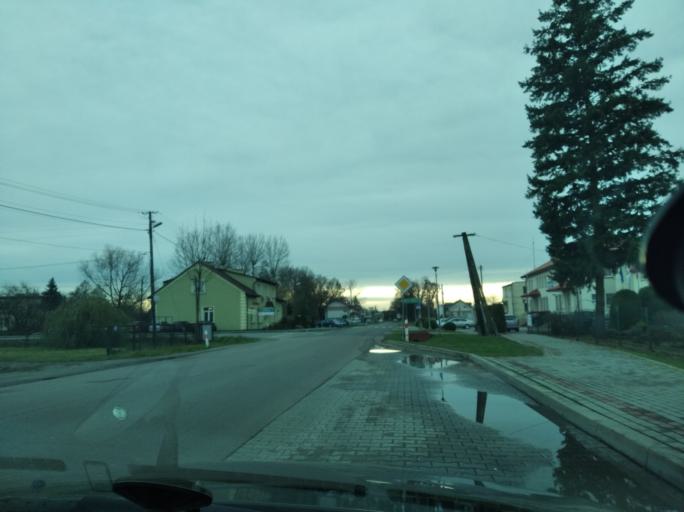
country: PL
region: Subcarpathian Voivodeship
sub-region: Powiat lancucki
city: Czarna
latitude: 50.0945
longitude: 22.1851
